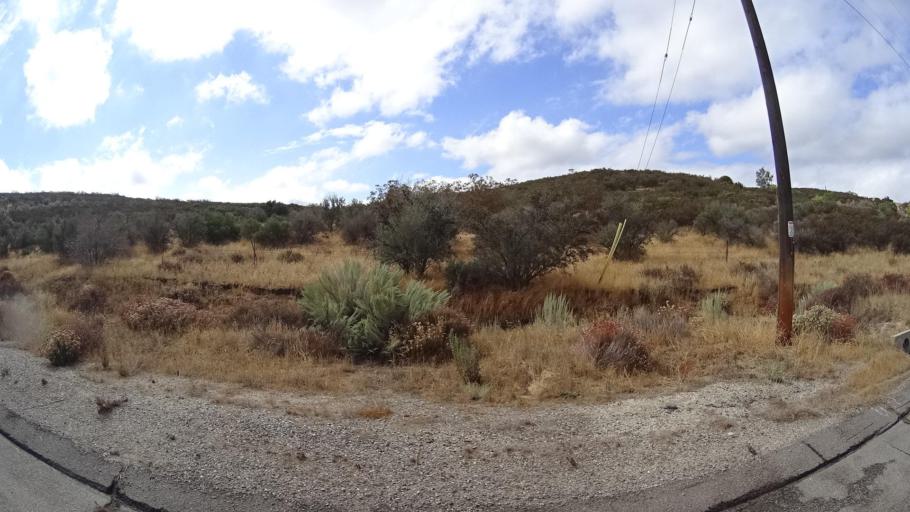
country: US
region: California
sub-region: San Diego County
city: Campo
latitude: 32.7193
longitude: -116.3946
